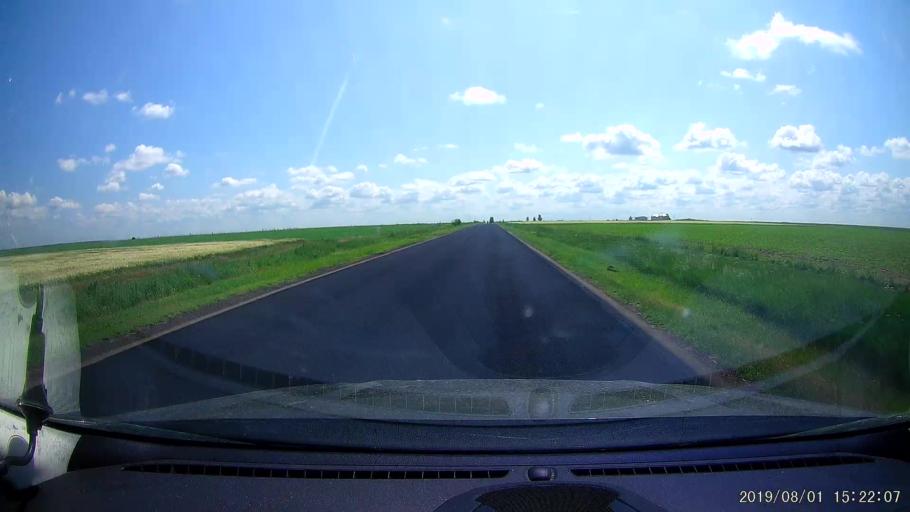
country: RO
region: Braila
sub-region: Comuna Tufesti
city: Tufesti
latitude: 45.0587
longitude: 27.7825
